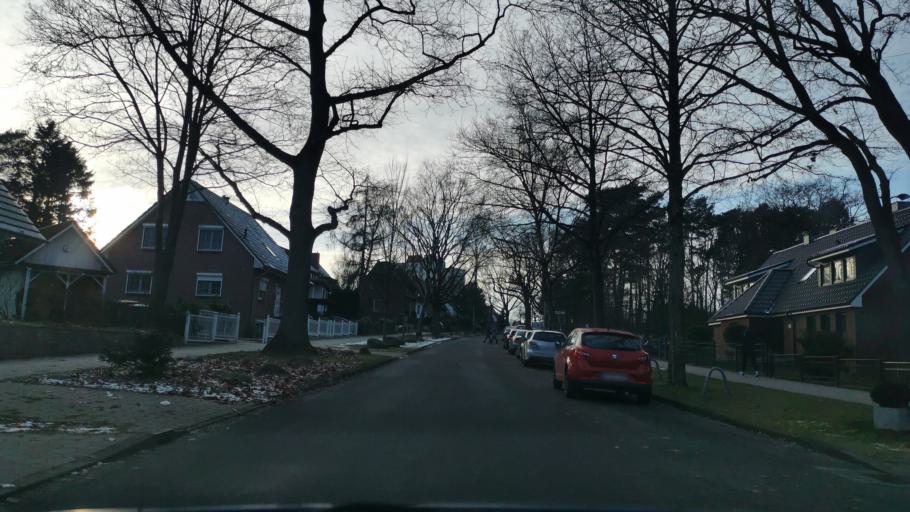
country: DE
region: Hamburg
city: Harburg
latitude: 53.4508
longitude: 9.9423
